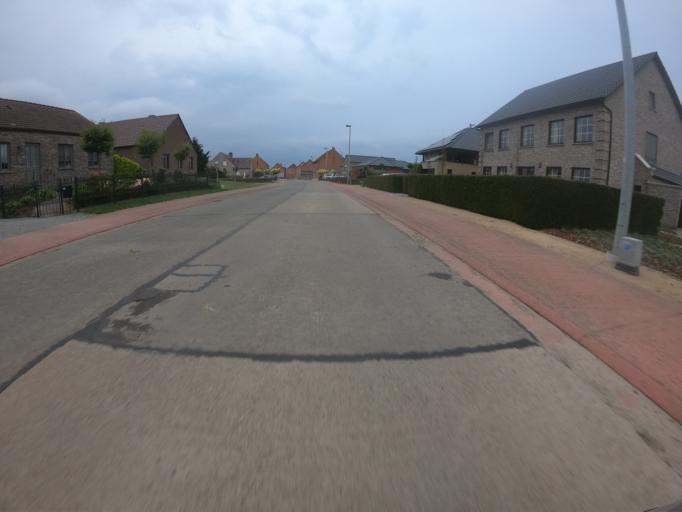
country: BE
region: Flanders
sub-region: Provincie Vlaams-Brabant
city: Scherpenheuvel-Zichem
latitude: 50.9880
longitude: 4.9214
